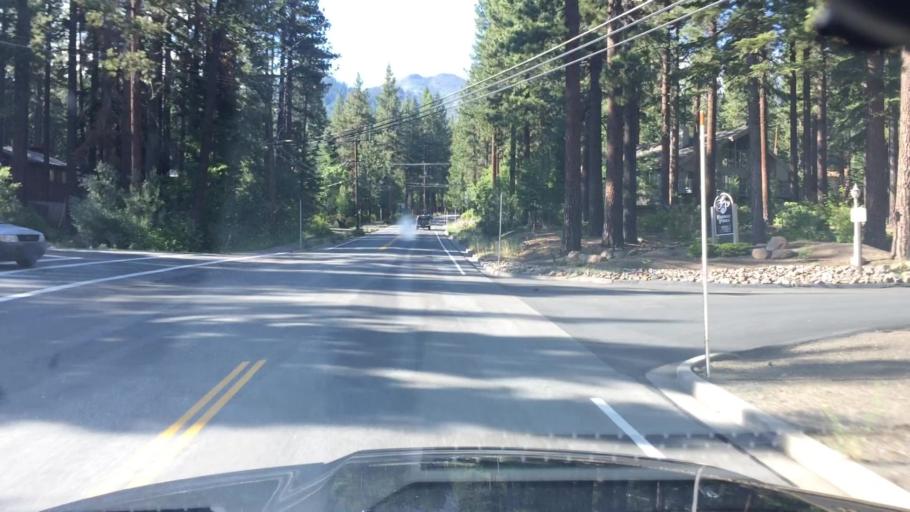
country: US
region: Nevada
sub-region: Washoe County
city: Incline Village
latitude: 39.2577
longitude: -119.9509
